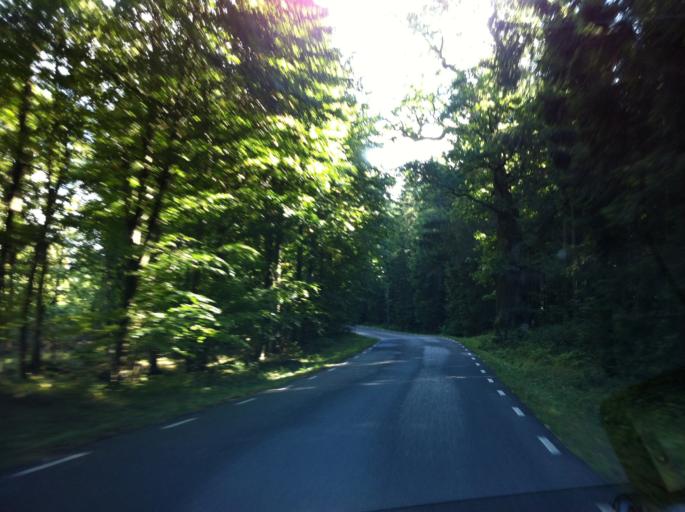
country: SE
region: Skane
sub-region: Kristianstads Kommun
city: Degeberga
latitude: 55.7489
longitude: 13.9429
